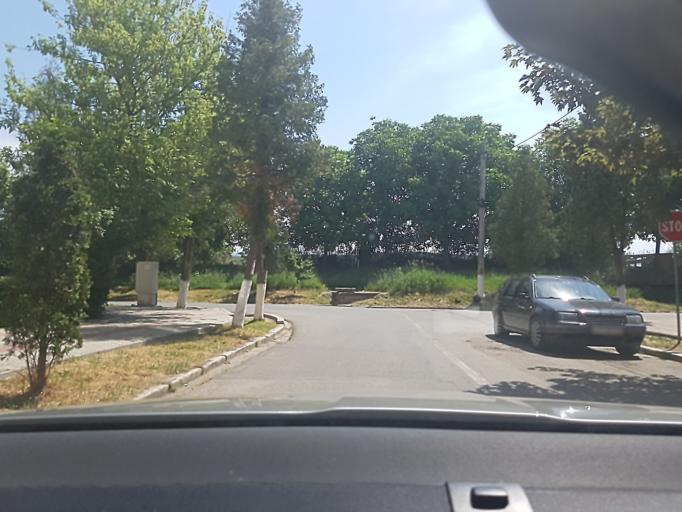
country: RO
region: Hunedoara
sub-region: Comuna Calan
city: Calan
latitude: 45.7307
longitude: 23.0300
